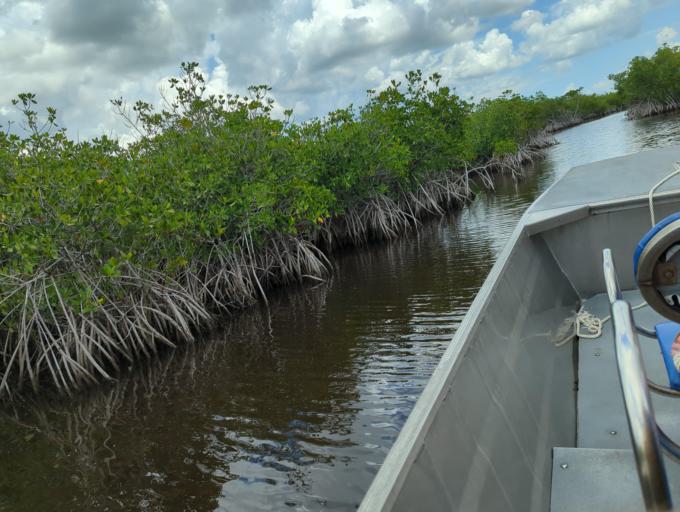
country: US
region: Florida
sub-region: Collier County
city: Marco
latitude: 25.9069
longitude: -81.3729
